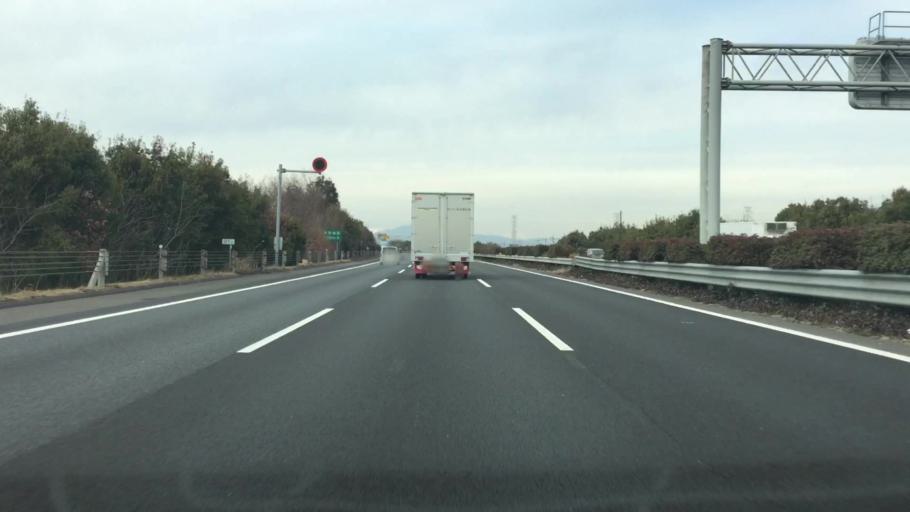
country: JP
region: Gunma
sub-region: Sawa-gun
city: Tamamura
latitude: 36.2961
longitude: 139.0969
